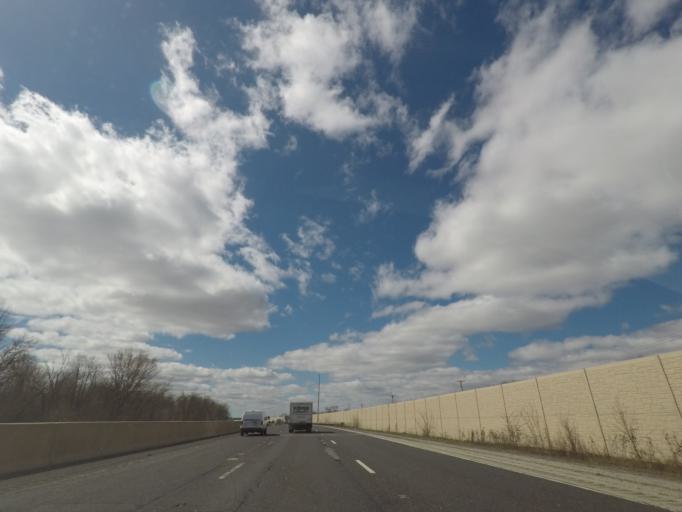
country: US
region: Illinois
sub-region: Will County
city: Crystal Lawns
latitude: 41.5755
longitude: -88.1786
